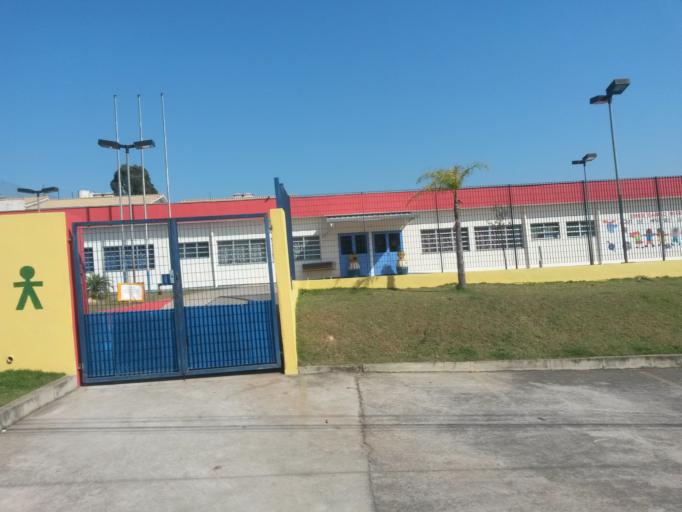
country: BR
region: Sao Paulo
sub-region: Sao Bernardo Do Campo
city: Sao Bernardo do Campo
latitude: -23.7051
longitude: -46.5720
